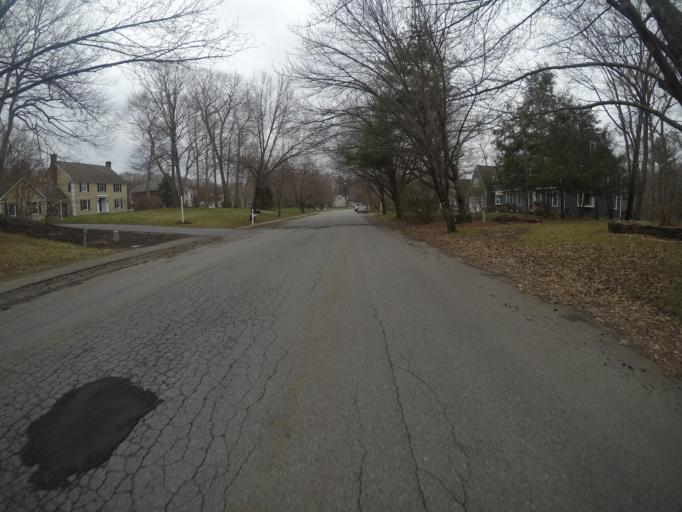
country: US
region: Massachusetts
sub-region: Bristol County
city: Easton
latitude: 42.0543
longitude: -71.1447
